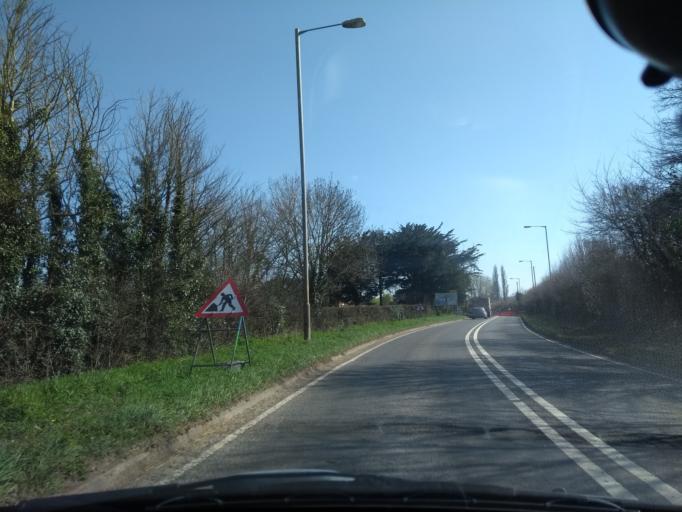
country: GB
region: England
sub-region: Somerset
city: Taunton
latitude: 51.0338
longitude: -3.1393
